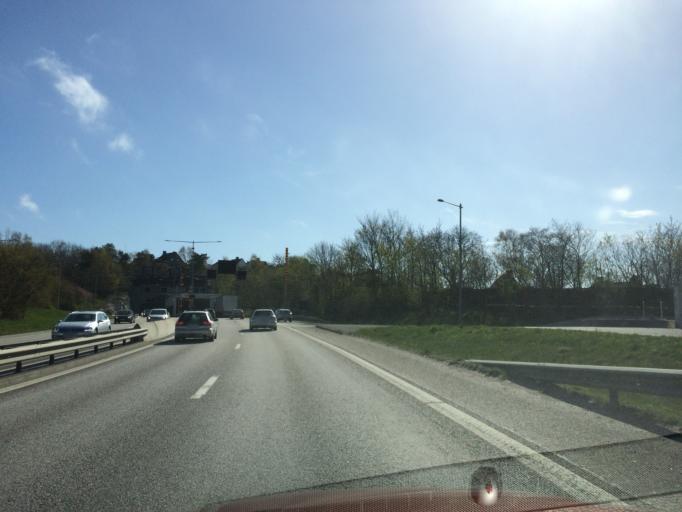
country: SE
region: Vaestra Goetaland
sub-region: Goteborg
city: Majorna
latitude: 57.6774
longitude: 11.8961
